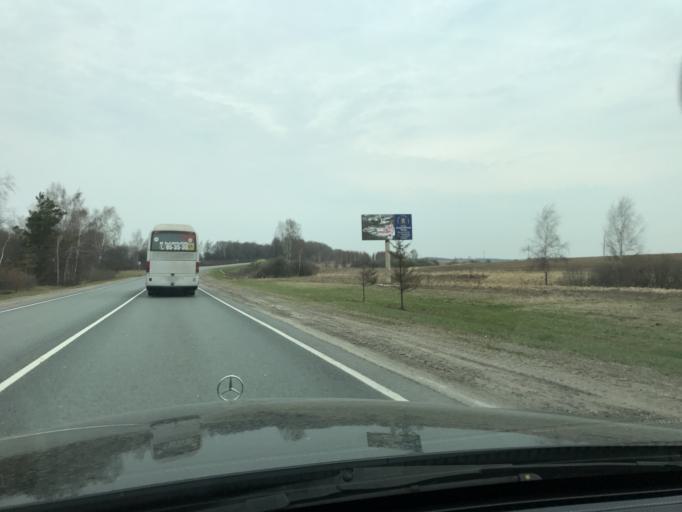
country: RU
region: Vladimir
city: Suzdal'
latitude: 56.3579
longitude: 40.4692
